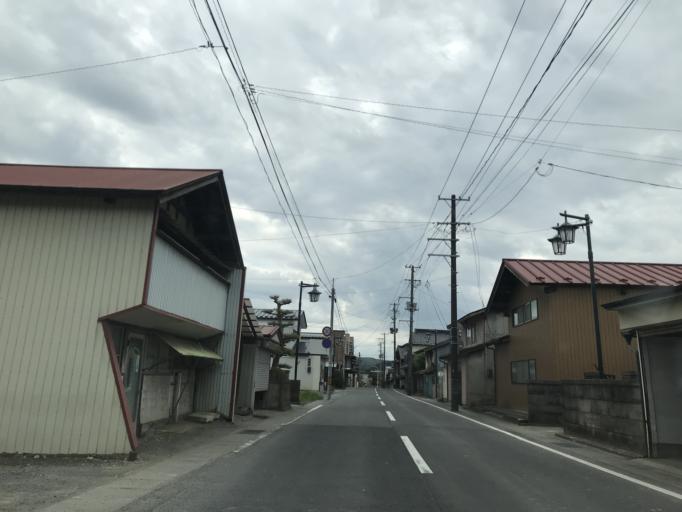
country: JP
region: Iwate
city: Ichinoseki
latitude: 38.7717
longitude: 141.3300
